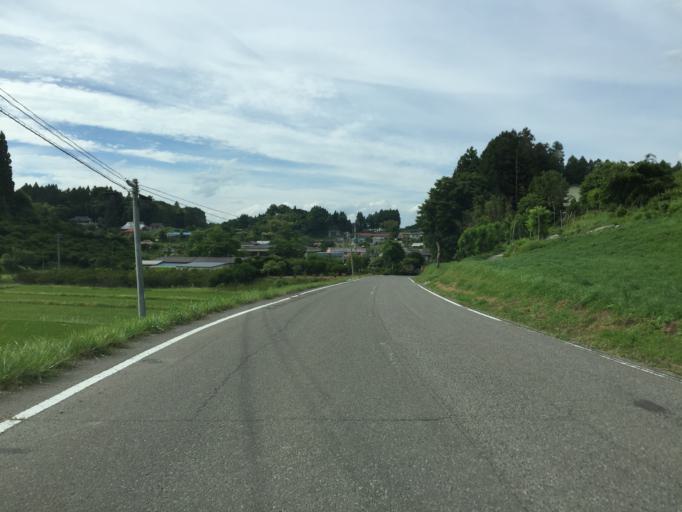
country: JP
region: Fukushima
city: Funehikimachi-funehiki
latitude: 37.5329
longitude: 140.5584
